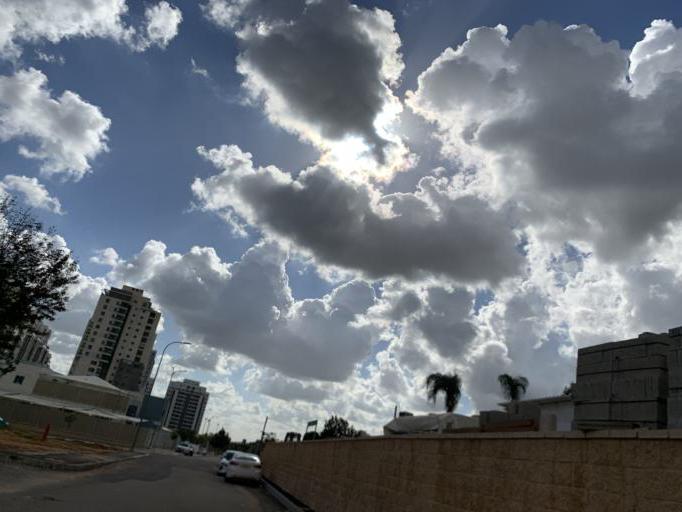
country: IL
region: Central District
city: Hod HaSharon
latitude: 32.1688
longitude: 34.8975
